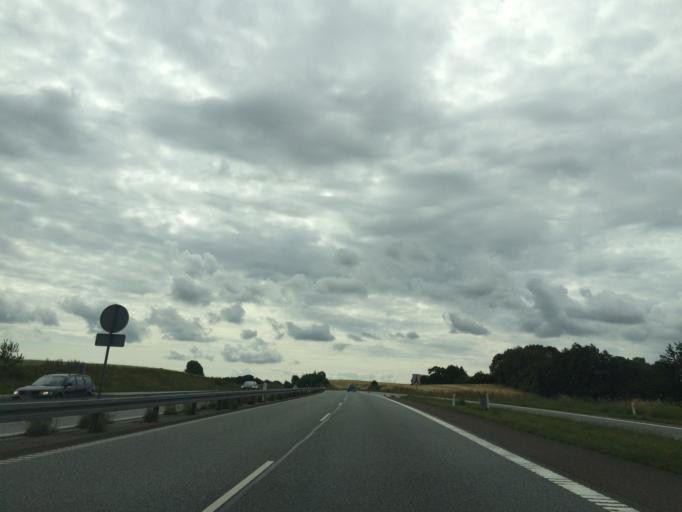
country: DK
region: Central Jutland
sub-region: Syddjurs Kommune
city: Ronde
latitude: 56.3017
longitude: 10.5086
